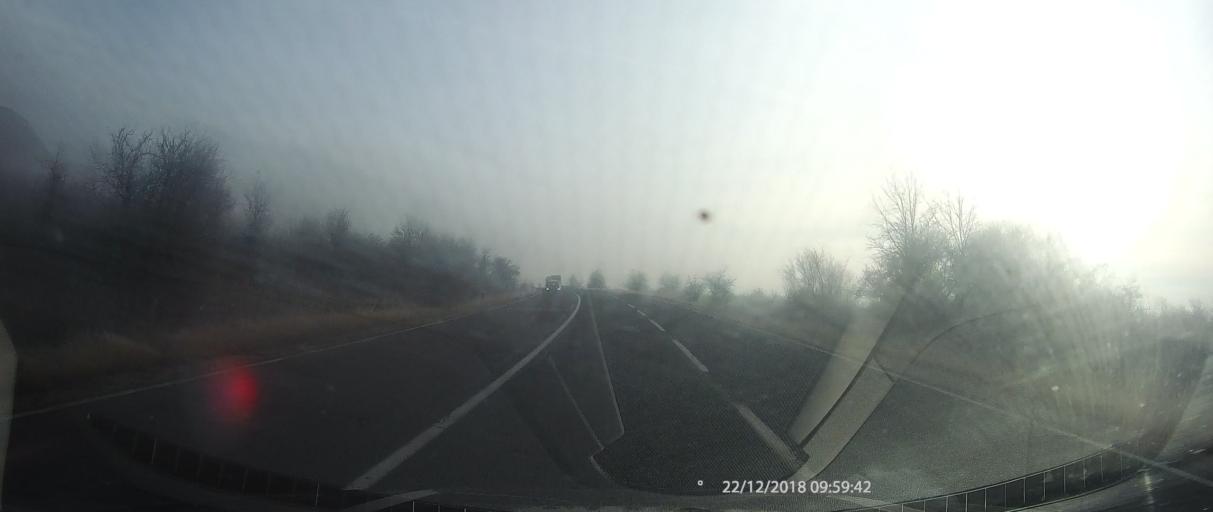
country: MK
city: Klechovce
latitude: 42.1497
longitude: 21.9644
